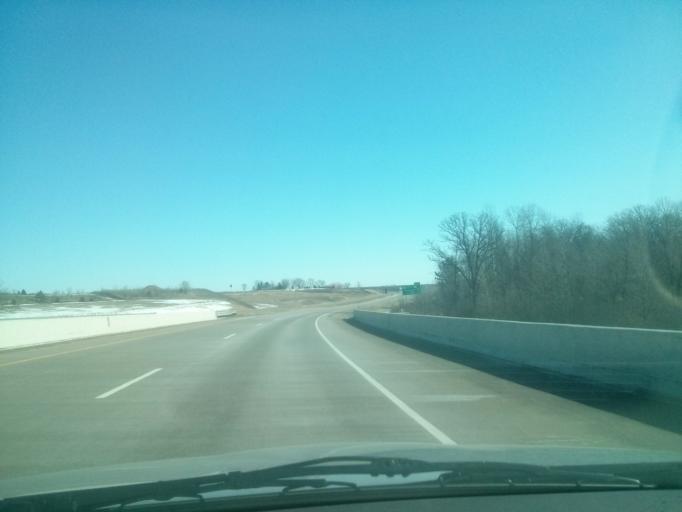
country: US
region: Wisconsin
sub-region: Saint Croix County
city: Somerset
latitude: 45.1177
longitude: -92.6628
